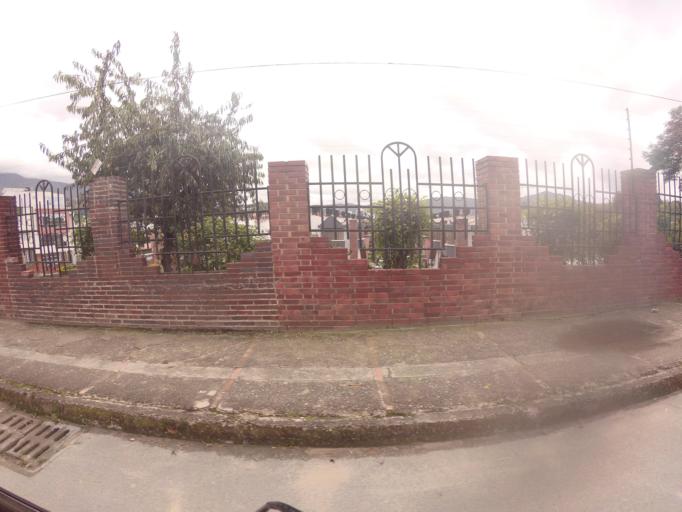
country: CO
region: Boyaca
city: Duitama
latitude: 5.8312
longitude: -73.0412
